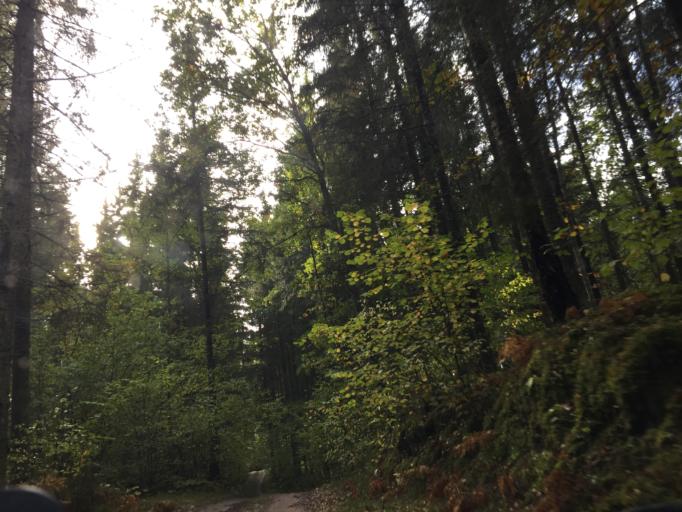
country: LV
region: Jaunpils
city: Jaunpils
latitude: 56.5924
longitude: 23.0113
